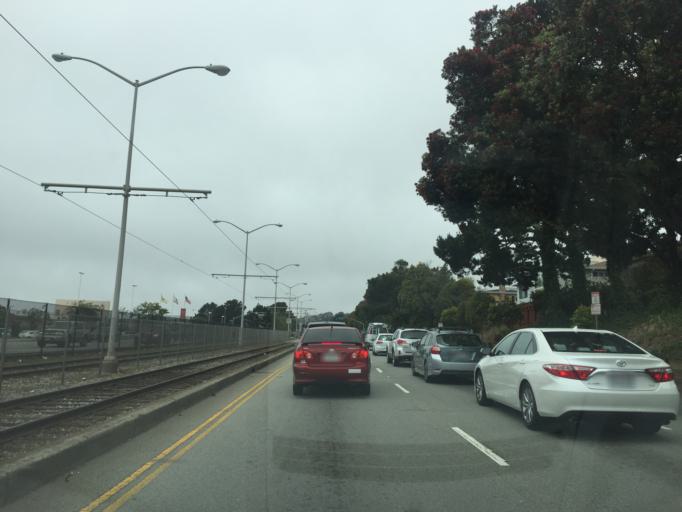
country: US
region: California
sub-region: San Mateo County
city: Daly City
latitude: 37.7253
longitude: -122.4749
